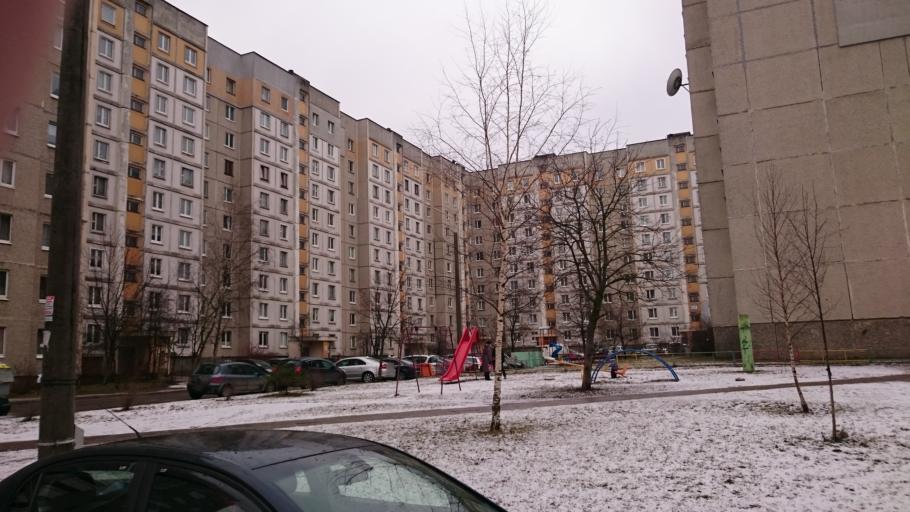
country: BY
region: Minsk
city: Borovlyany
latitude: 53.9398
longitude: 27.6857
